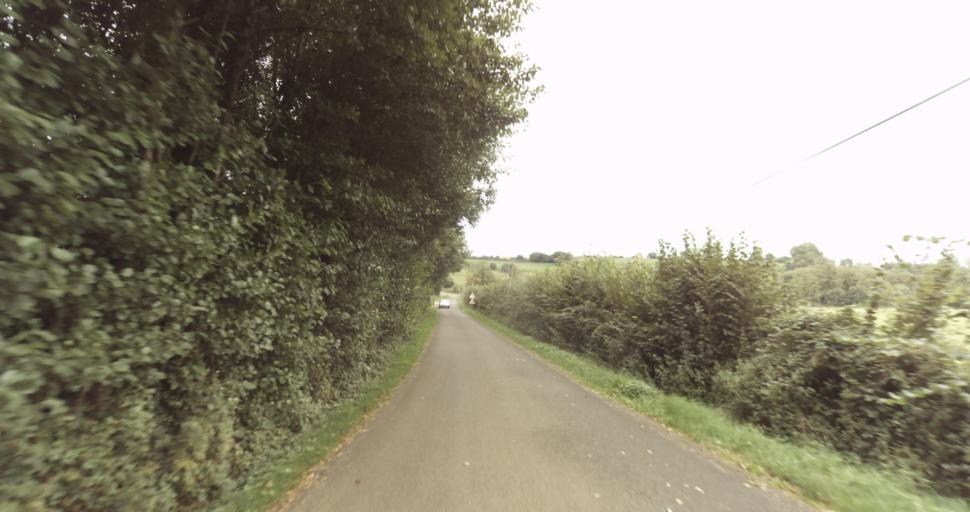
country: FR
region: Lower Normandy
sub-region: Departement de l'Orne
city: Gace
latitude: 48.7655
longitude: 0.3306
